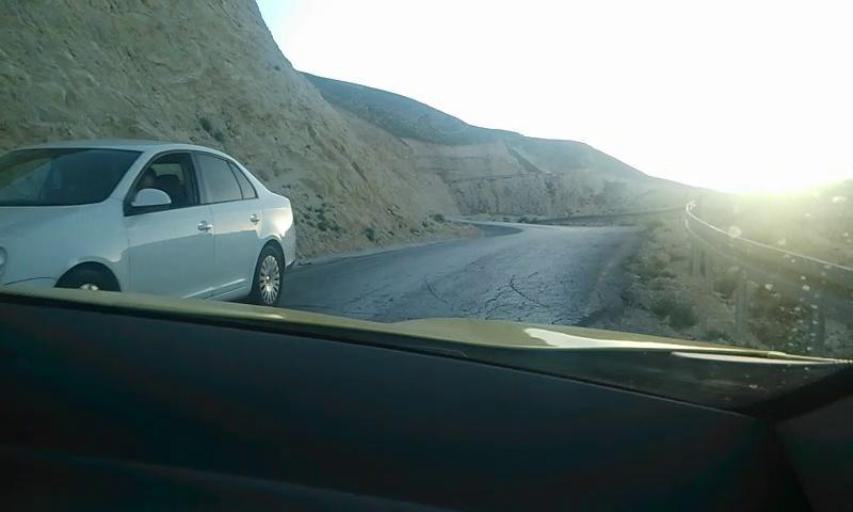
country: PS
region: West Bank
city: An Nuway`imah
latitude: 31.9121
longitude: 35.3829
